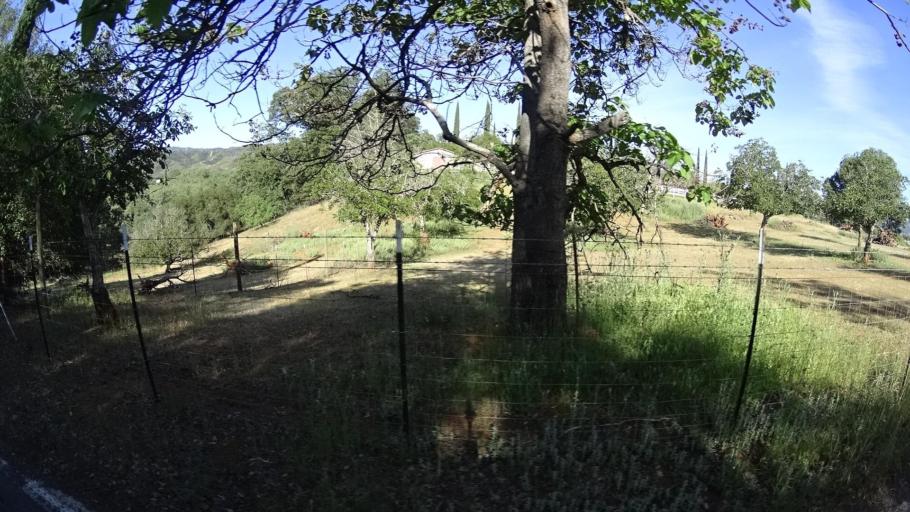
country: US
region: California
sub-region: Lake County
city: Lakeport
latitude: 39.0436
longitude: -122.9508
